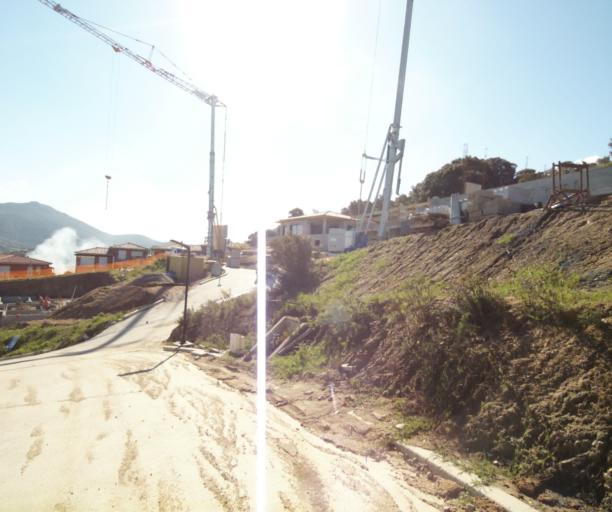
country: FR
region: Corsica
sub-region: Departement de la Corse-du-Sud
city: Propriano
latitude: 41.6682
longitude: 8.9067
